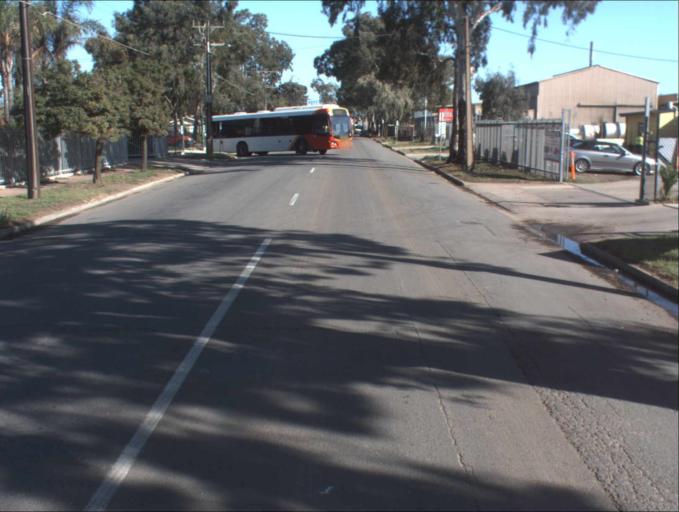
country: AU
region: South Australia
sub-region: Port Adelaide Enfield
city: Alberton
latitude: -34.8415
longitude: 138.5425
